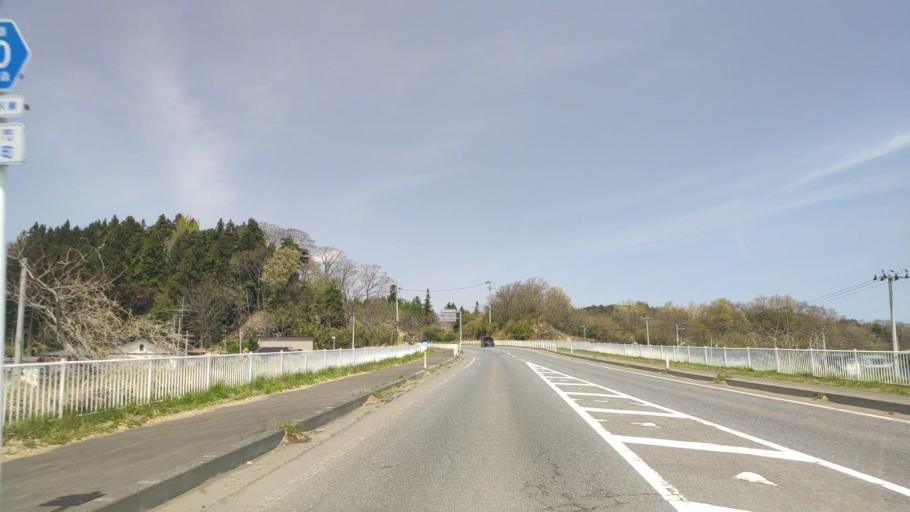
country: JP
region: Aomori
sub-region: Hachinohe Shi
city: Uchimaru
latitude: 40.5184
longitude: 141.4266
